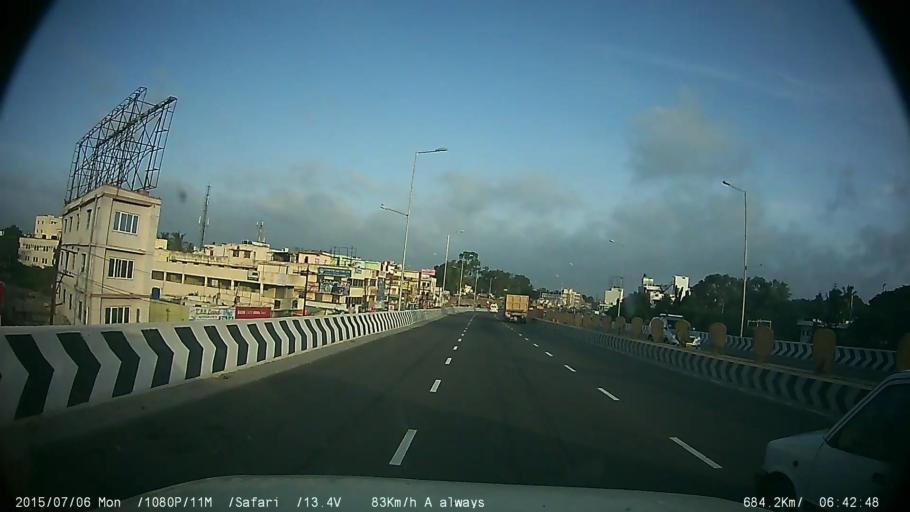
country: IN
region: Tamil Nadu
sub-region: Krishnagiri
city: Hosur
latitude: 12.7359
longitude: 77.8266
